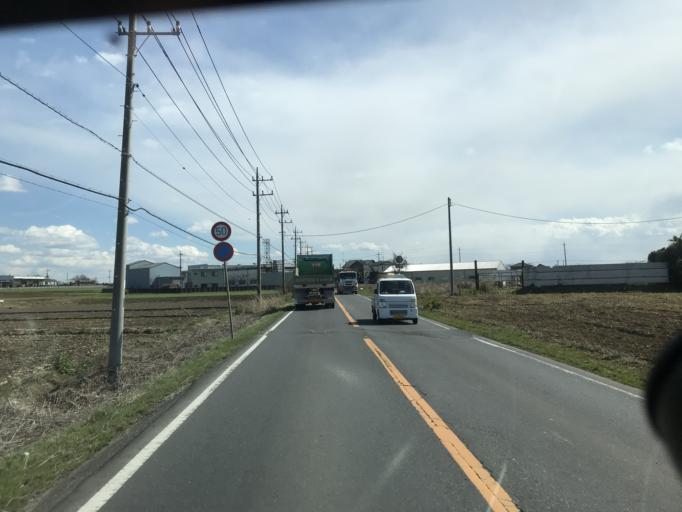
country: JP
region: Ibaraki
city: Yuki
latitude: 36.2425
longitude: 139.9292
